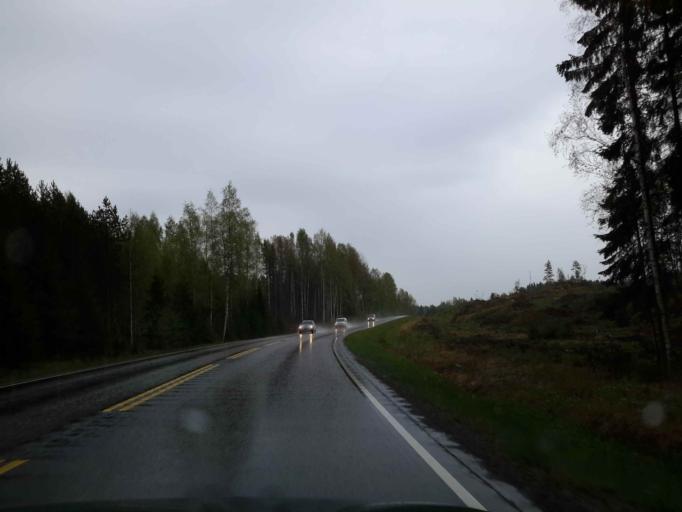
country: FI
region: Uusimaa
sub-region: Helsinki
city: Vihti
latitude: 60.3916
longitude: 24.4949
